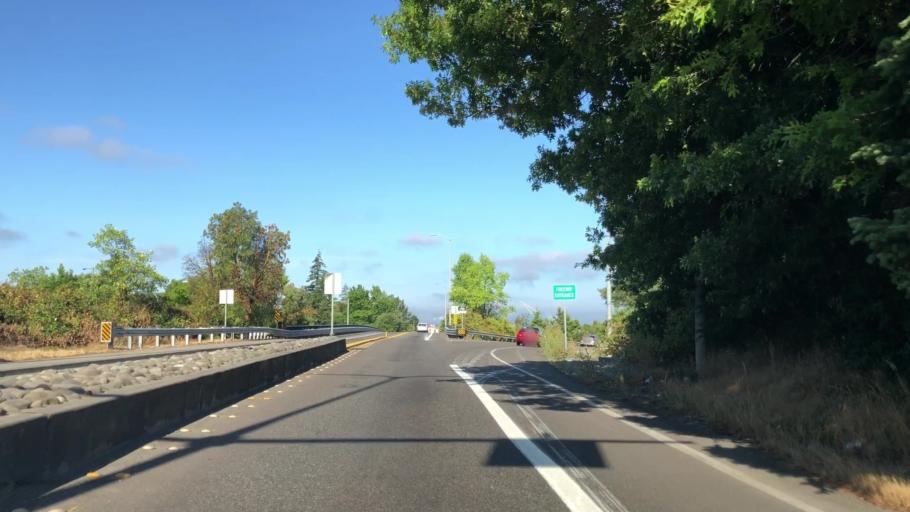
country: US
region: Washington
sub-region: King County
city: SeaTac
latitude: 47.4652
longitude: -122.2972
